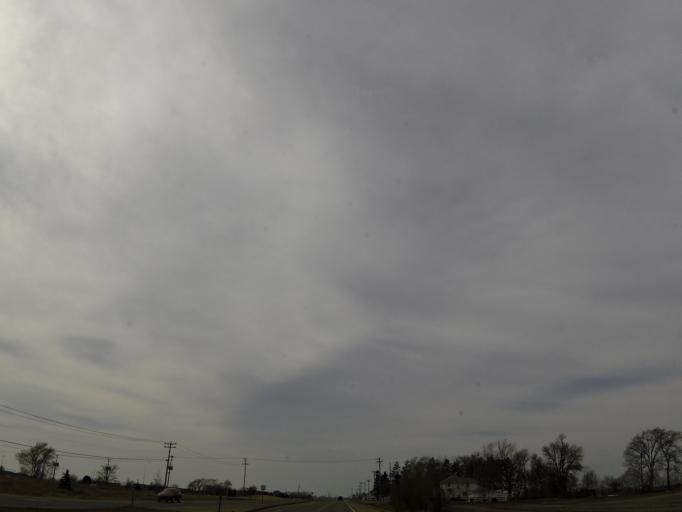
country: US
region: Minnesota
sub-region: Dakota County
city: Rosemount
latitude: 44.7391
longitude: -93.0682
